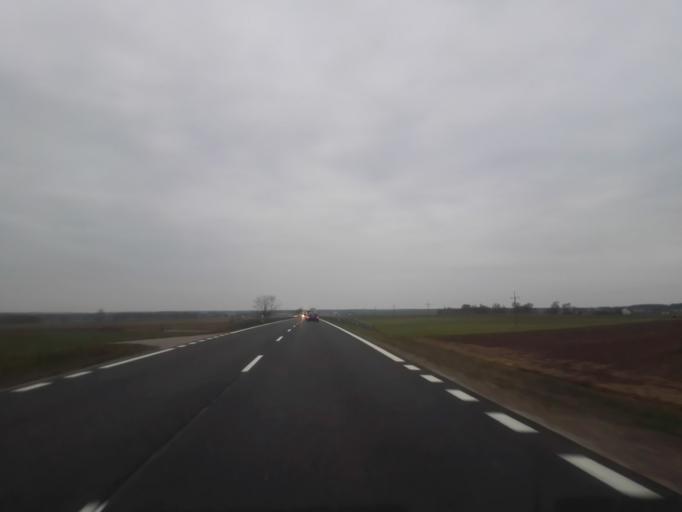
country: PL
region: Podlasie
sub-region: Powiat kolnenski
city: Stawiski
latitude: 53.4100
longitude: 22.1613
